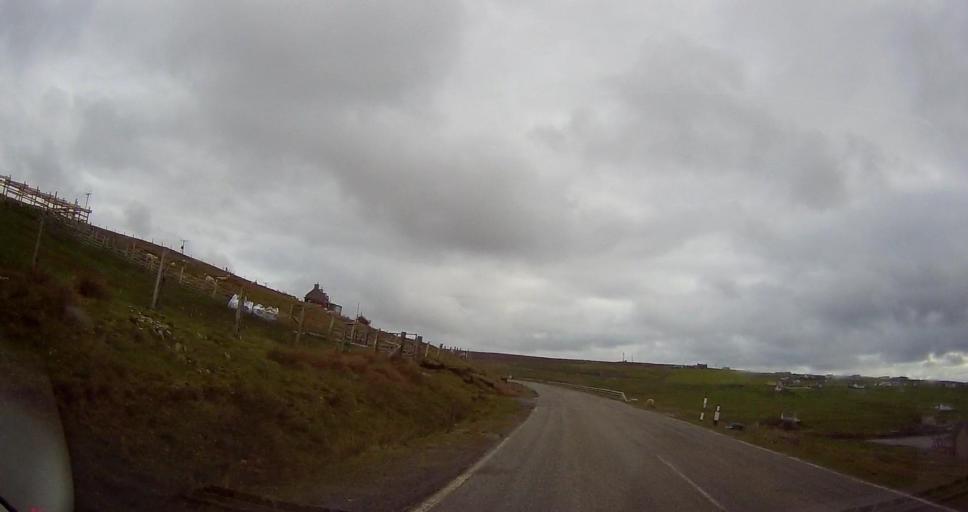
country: GB
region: Scotland
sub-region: Shetland Islands
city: Shetland
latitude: 60.6093
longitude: -1.0753
